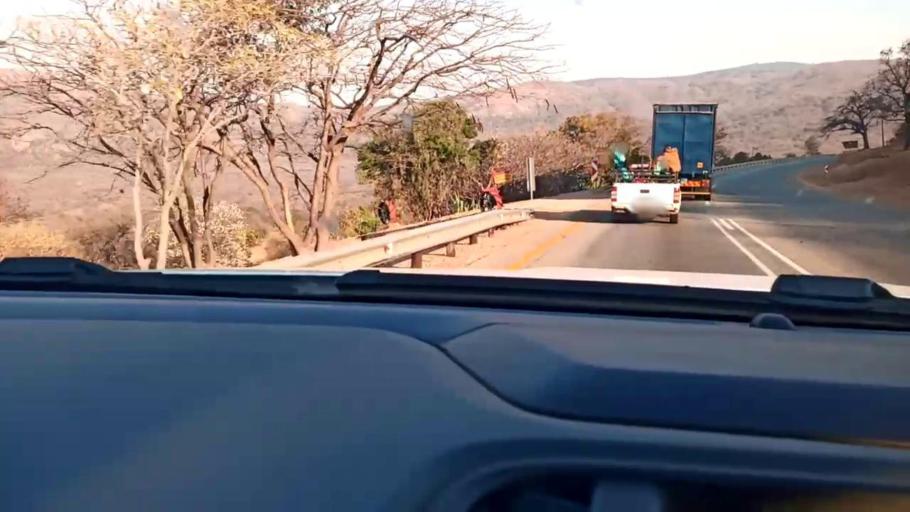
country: ZA
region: Limpopo
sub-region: Mopani District Municipality
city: Ga-Kgapane
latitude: -23.6486
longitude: 30.1715
